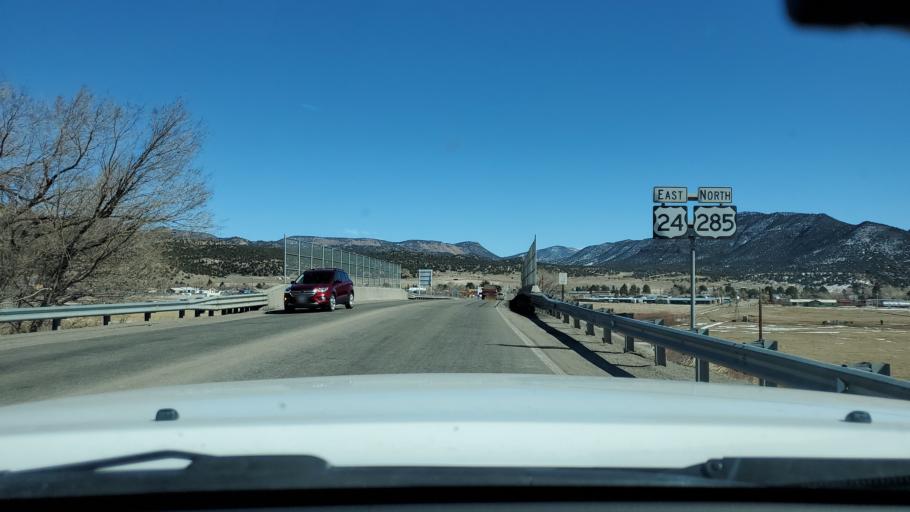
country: US
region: Colorado
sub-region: Chaffee County
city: Buena Vista
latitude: 38.8101
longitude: -106.1145
